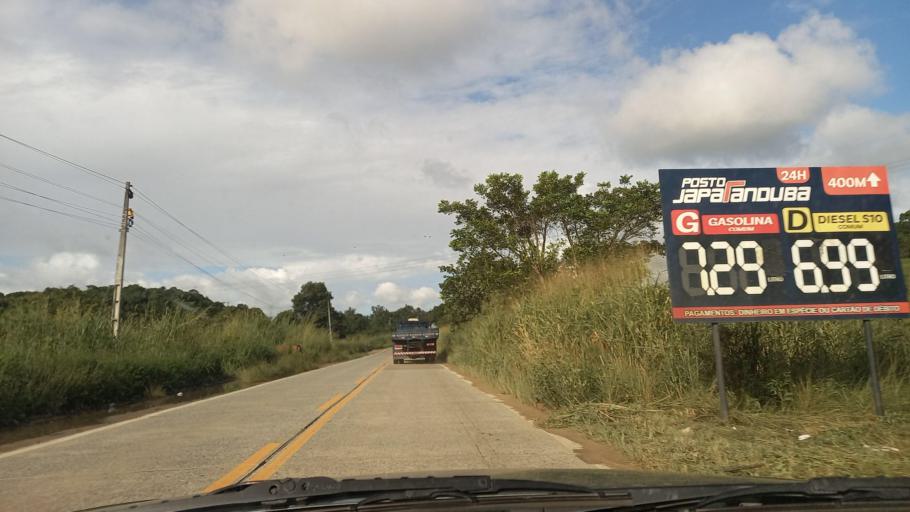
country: BR
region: Pernambuco
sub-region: Palmares
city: Palmares
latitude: -8.6910
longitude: -35.6136
